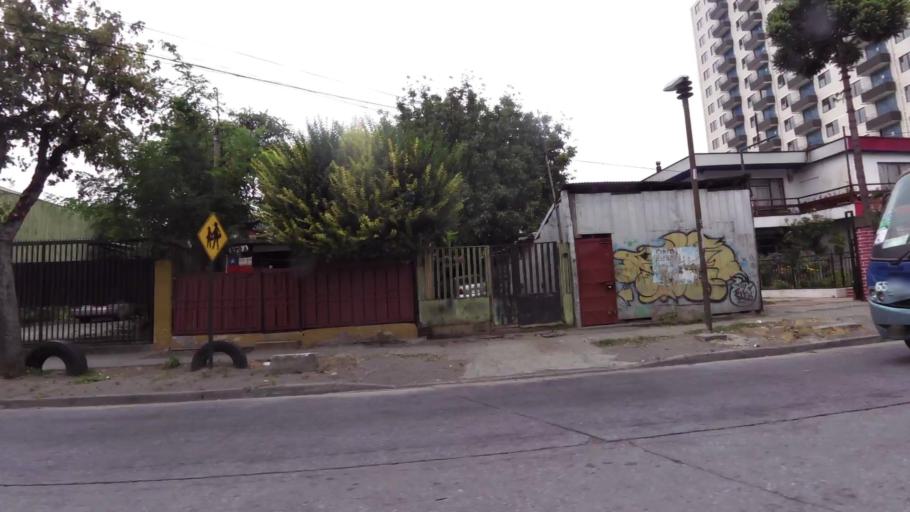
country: CL
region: Biobio
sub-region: Provincia de Concepcion
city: Concepcion
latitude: -36.8121
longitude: -73.0368
